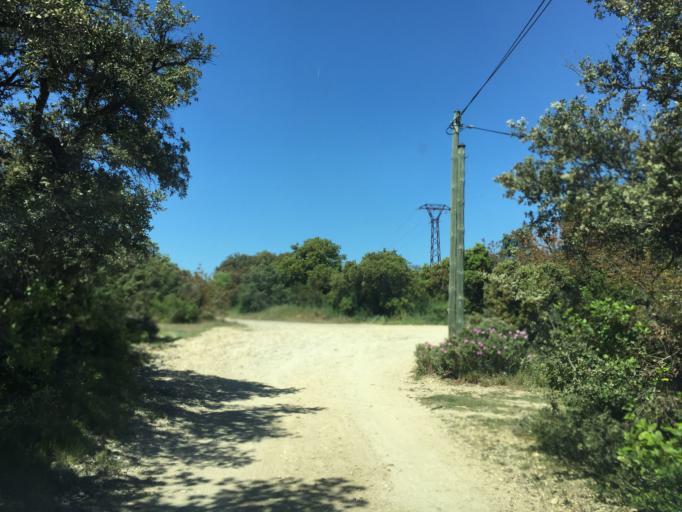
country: FR
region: Provence-Alpes-Cote d'Azur
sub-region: Departement du Vaucluse
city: Chateauneuf-du-Pape
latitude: 44.0548
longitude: 4.8125
